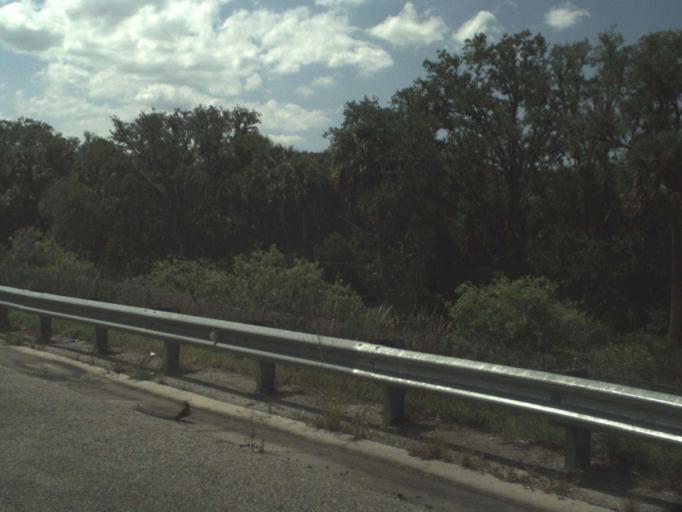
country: US
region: Florida
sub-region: Brevard County
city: Cocoa West
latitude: 28.3707
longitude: -80.8911
